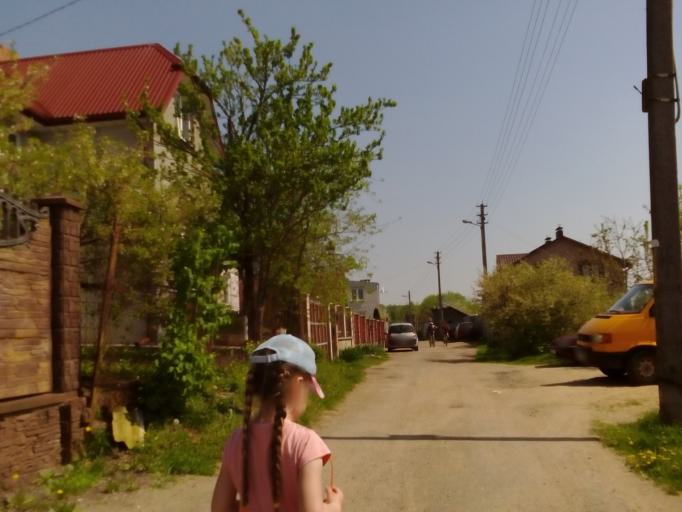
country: BY
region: Grodnenskaya
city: Hrodna
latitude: 53.6649
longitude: 23.8520
